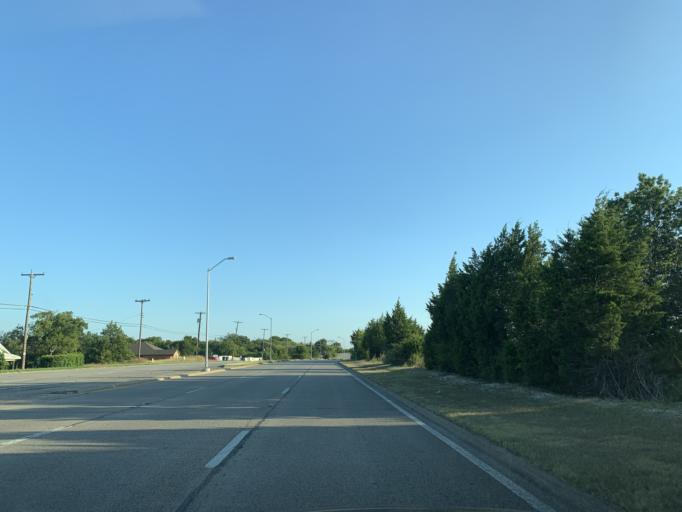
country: US
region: Texas
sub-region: Dallas County
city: Hutchins
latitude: 32.6697
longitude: -96.7831
